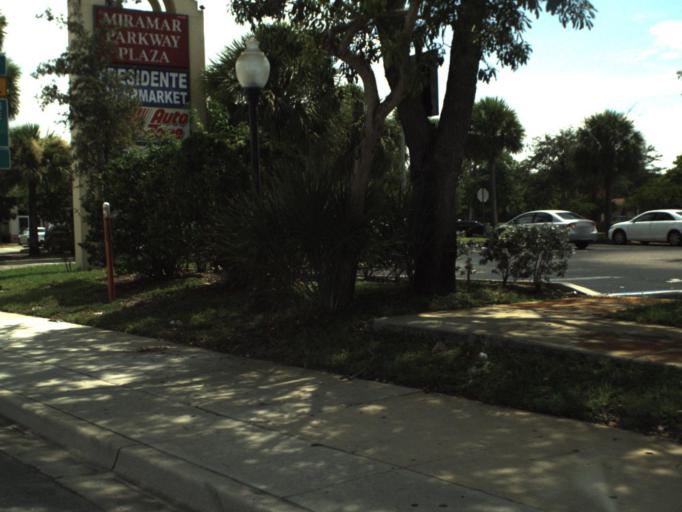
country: US
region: Florida
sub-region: Miami-Dade County
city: Lake Lucerne
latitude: 25.9801
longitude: -80.2473
